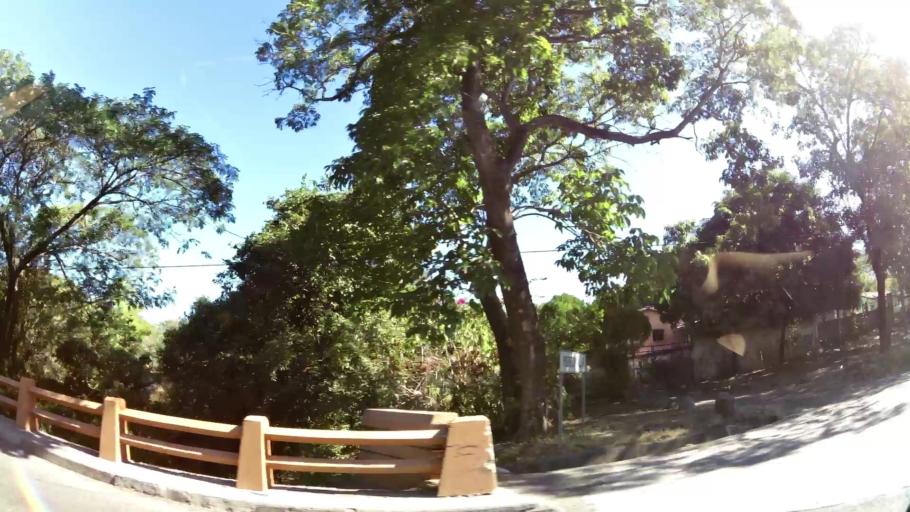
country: SV
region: San Miguel
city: San Miguel
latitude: 13.4496
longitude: -88.1351
